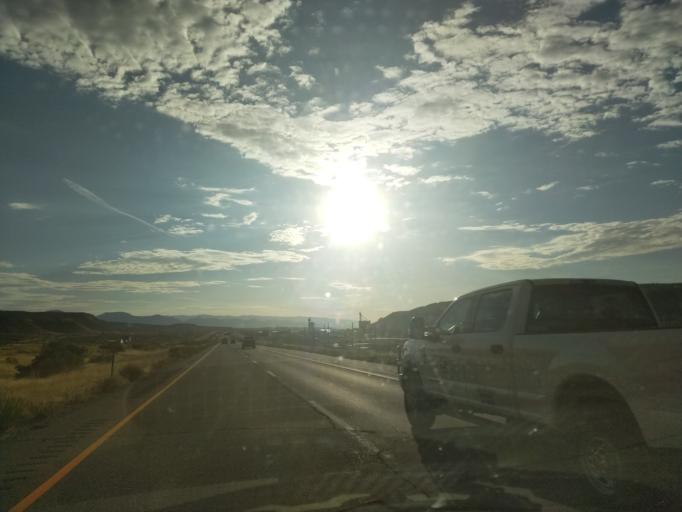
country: US
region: Colorado
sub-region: Garfield County
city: Rifle
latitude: 39.5131
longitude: -107.8675
